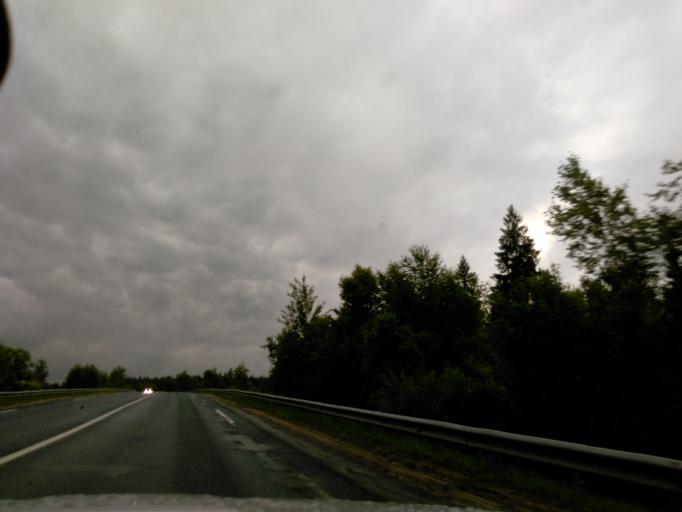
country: RU
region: Moskovskaya
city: Povarovo
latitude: 55.9911
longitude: 37.0428
